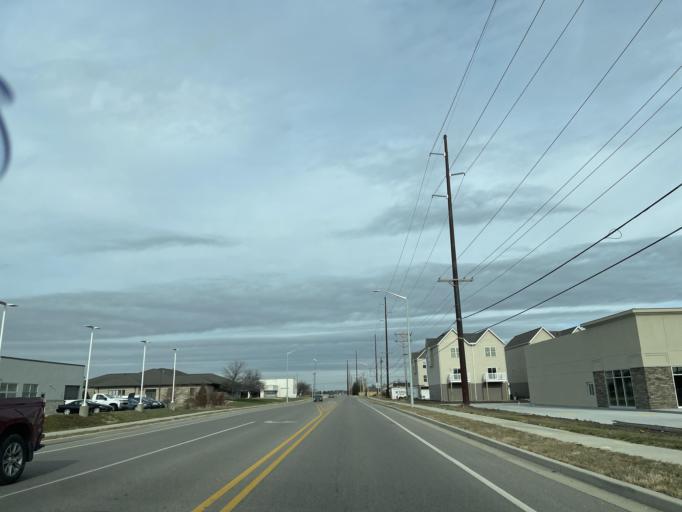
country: US
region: Illinois
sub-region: Sangamon County
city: Jerome
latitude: 39.7576
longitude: -89.7343
